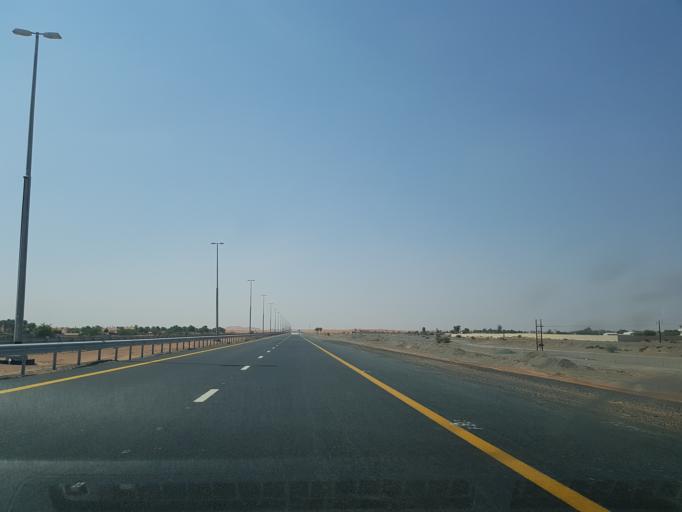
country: AE
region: Ash Shariqah
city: Adh Dhayd
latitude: 25.2362
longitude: 55.9021
